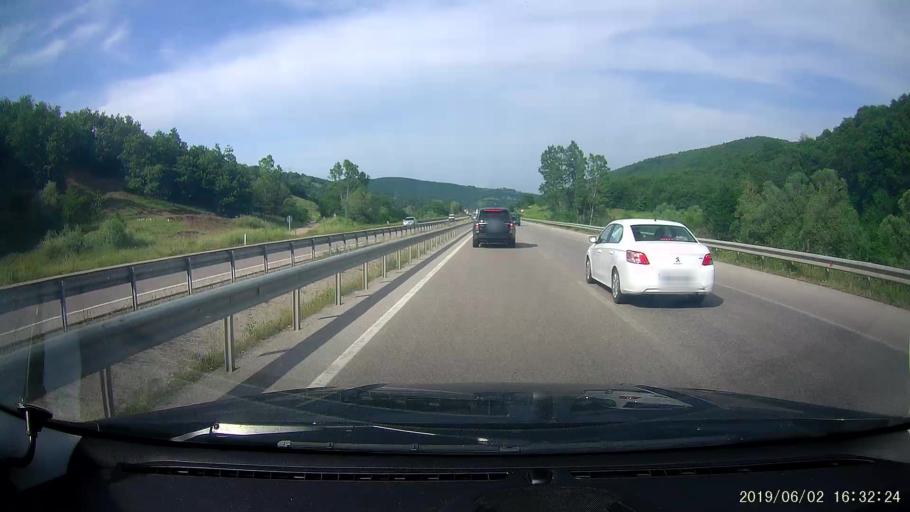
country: TR
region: Samsun
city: Kavak
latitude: 41.0397
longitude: 35.9200
